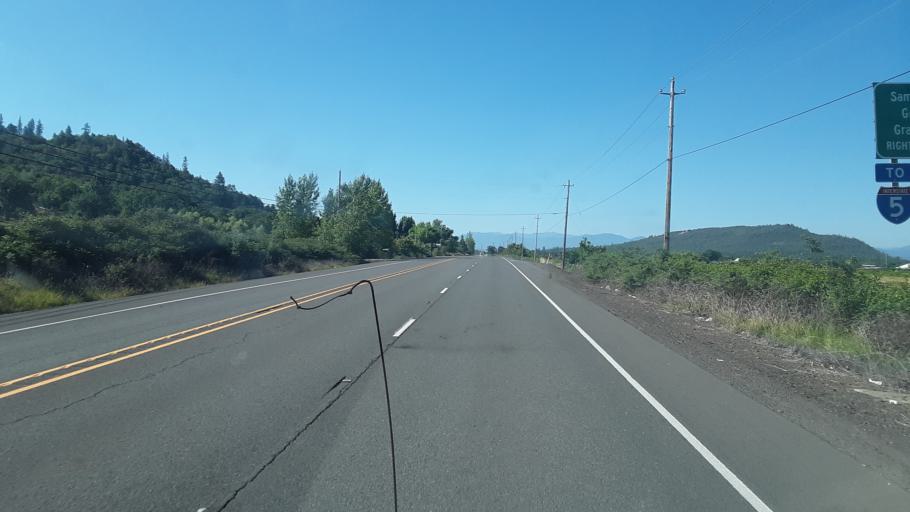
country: US
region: Oregon
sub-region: Jackson County
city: Eagle Point
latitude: 42.5321
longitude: -122.8143
